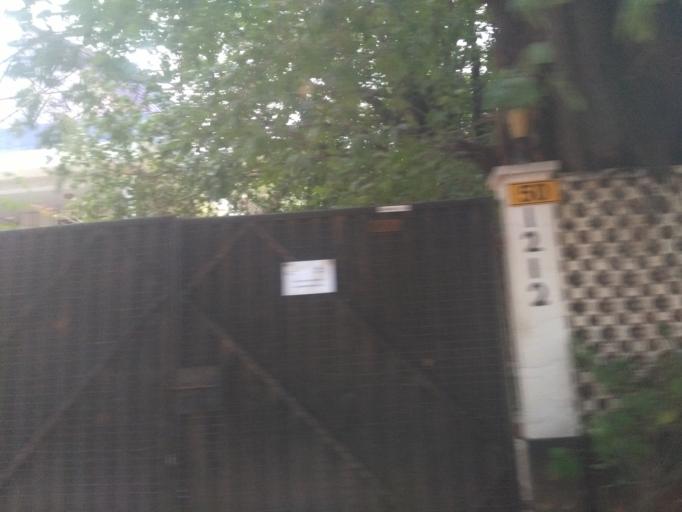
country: TZ
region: Dar es Salaam
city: Magomeni
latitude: -6.7489
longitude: 39.2736
